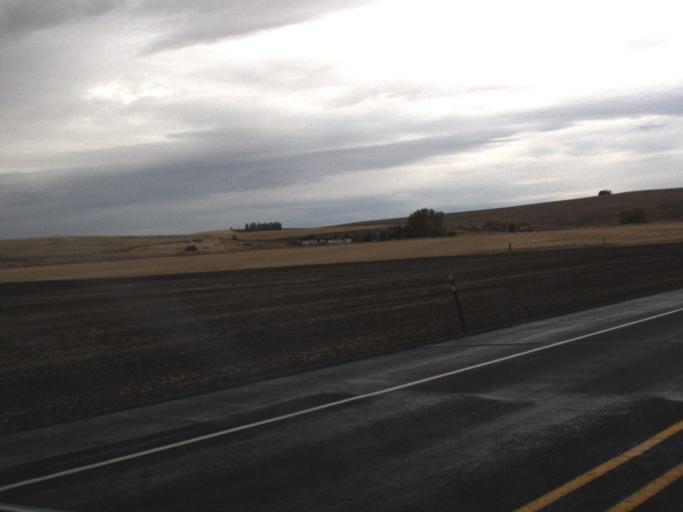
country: US
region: Washington
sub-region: Asotin County
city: Clarkston
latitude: 46.5458
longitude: -117.0925
